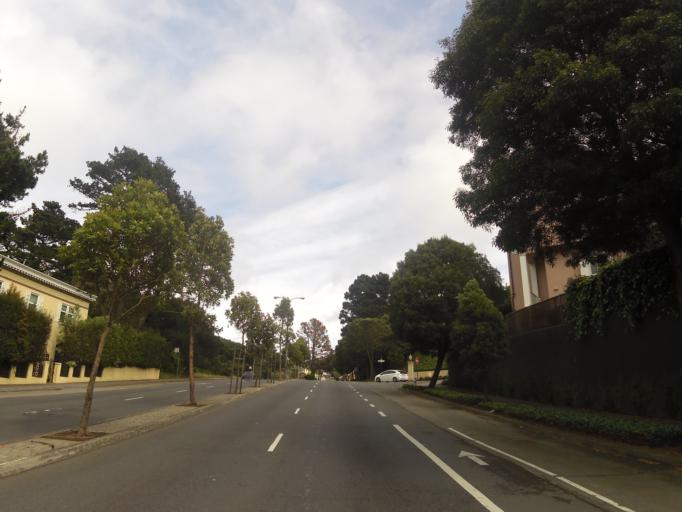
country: US
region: California
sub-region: San Mateo County
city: Daly City
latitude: 37.7400
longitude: -122.4635
